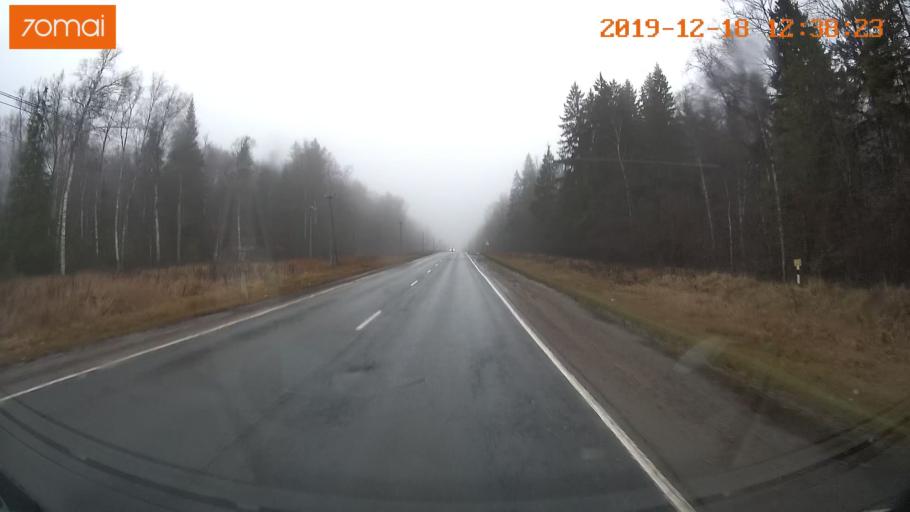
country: RU
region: Moskovskaya
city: Vysokovsk
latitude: 56.1511
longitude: 36.6046
